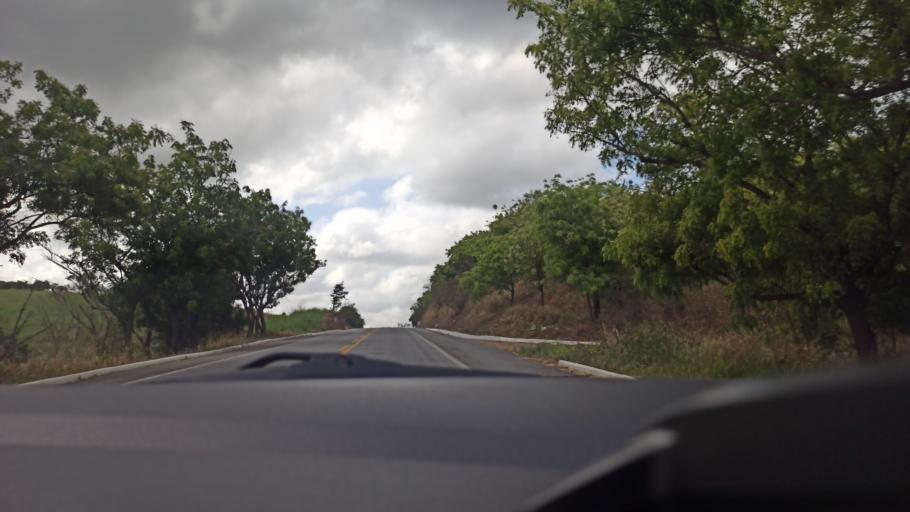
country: BR
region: Pernambuco
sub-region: Timbauba
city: Timbauba
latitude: -7.5331
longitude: -35.2889
